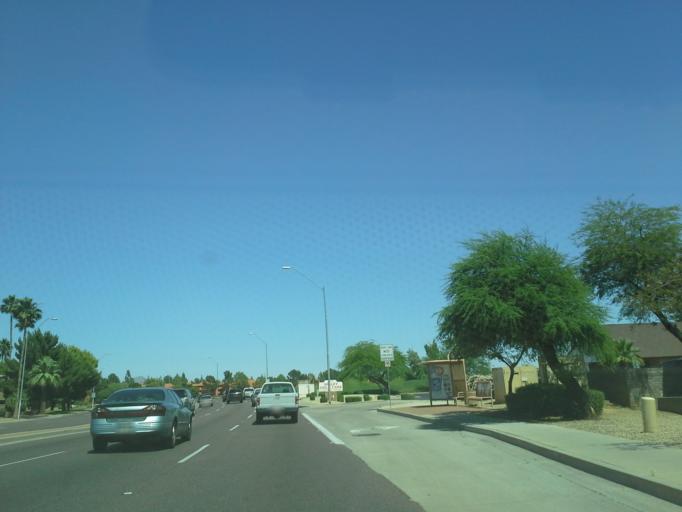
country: US
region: Arizona
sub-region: Maricopa County
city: Paradise Valley
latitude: 33.5970
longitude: -111.9954
